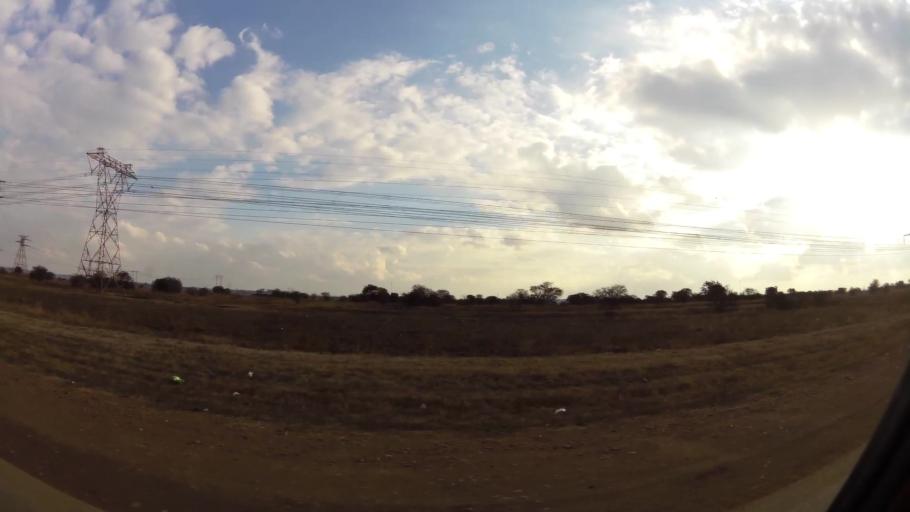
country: ZA
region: Gauteng
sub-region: Sedibeng District Municipality
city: Vereeniging
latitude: -26.6443
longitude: 27.8747
